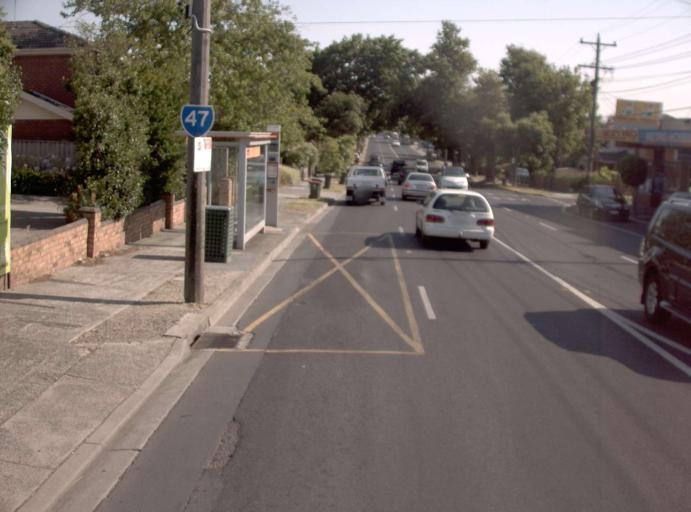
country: AU
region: Victoria
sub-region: Whitehorse
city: Box Hill South
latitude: -37.8283
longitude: 145.1218
